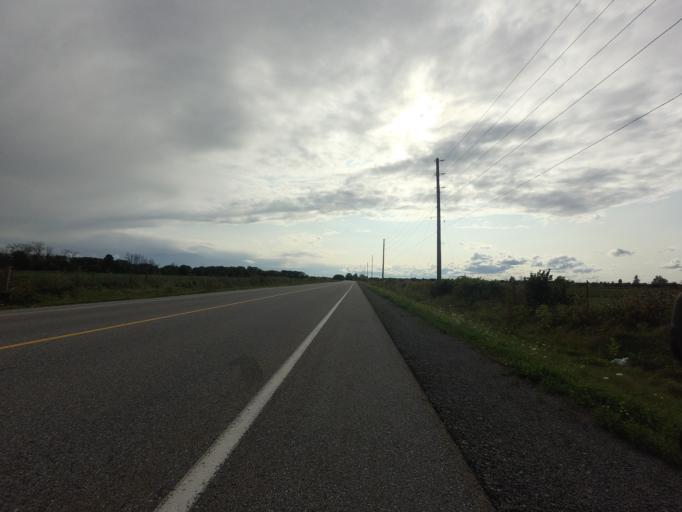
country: CA
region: Ontario
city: Bells Corners
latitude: 45.2948
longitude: -75.7197
